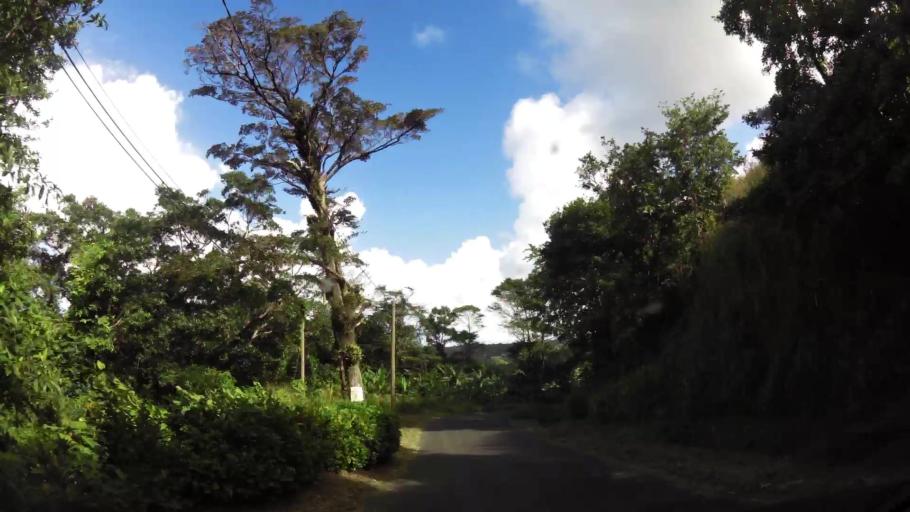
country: DM
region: Saint Andrew
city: Calibishie
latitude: 15.5946
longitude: -61.3879
